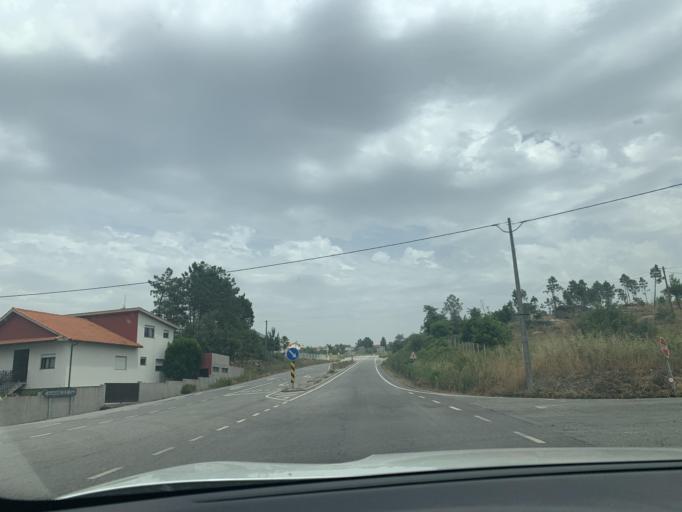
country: PT
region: Viseu
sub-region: Mangualde
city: Mangualde
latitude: 40.5843
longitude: -7.7561
